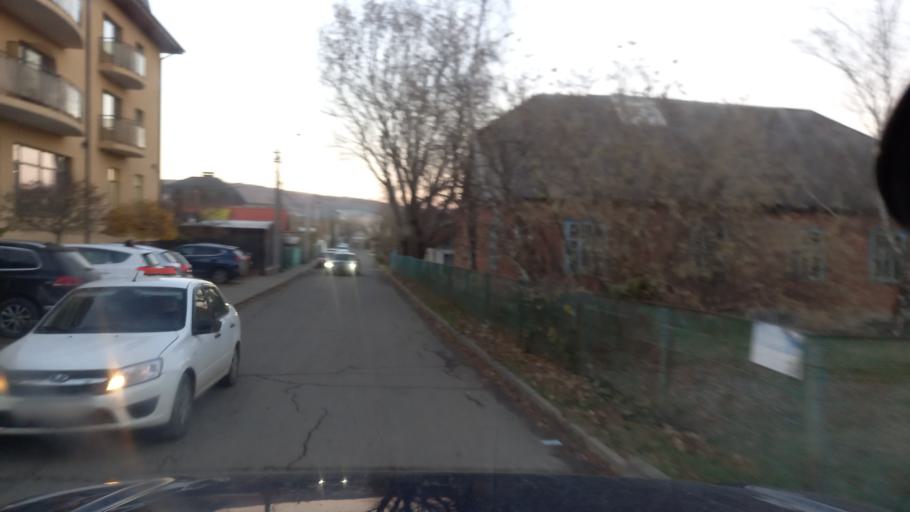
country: RU
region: Krasnodarskiy
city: Goryachiy Klyuch
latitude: 44.6262
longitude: 39.1029
